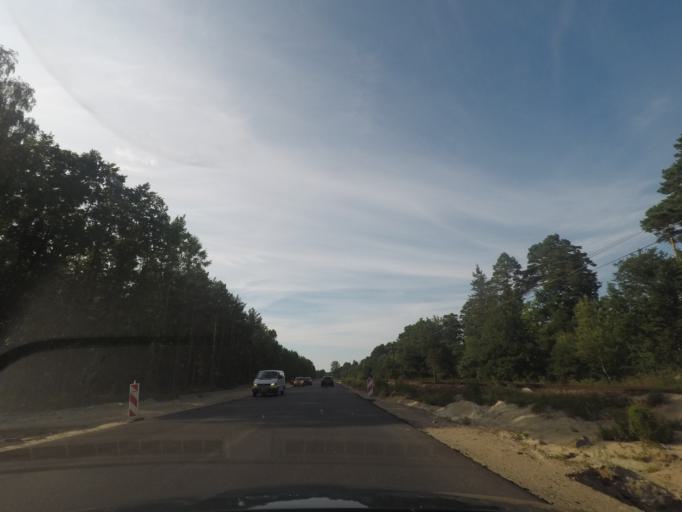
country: PL
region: Pomeranian Voivodeship
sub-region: Powiat leborski
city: Leba
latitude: 54.7195
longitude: 17.5739
